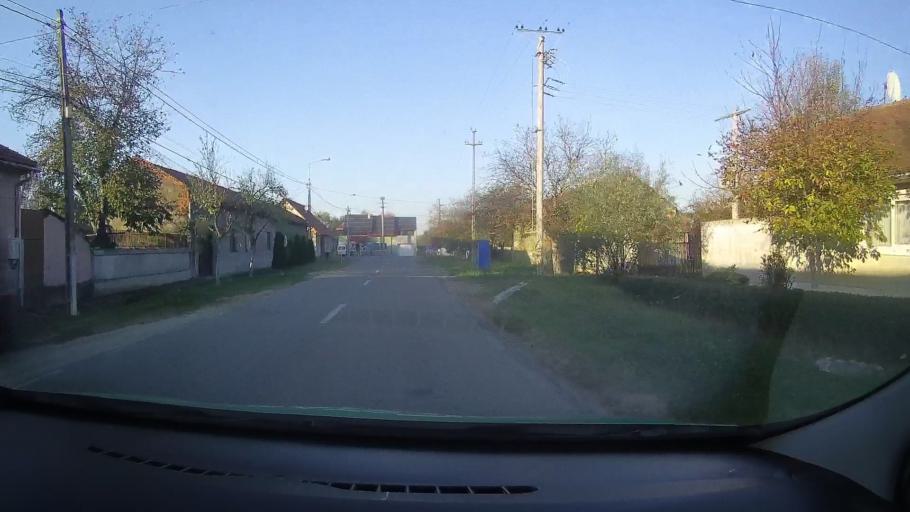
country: RO
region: Timis
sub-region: Comuna Fardea
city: Fardea
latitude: 45.7404
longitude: 22.1647
